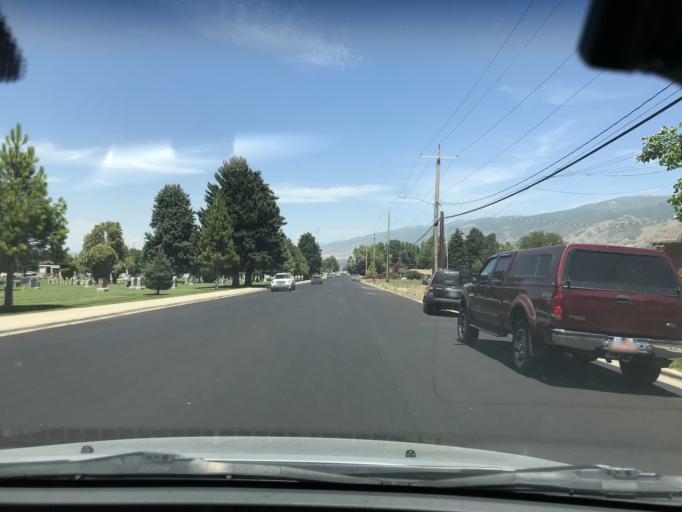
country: US
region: Utah
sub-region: Davis County
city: Woods Cross
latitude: 40.8666
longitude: -111.8857
